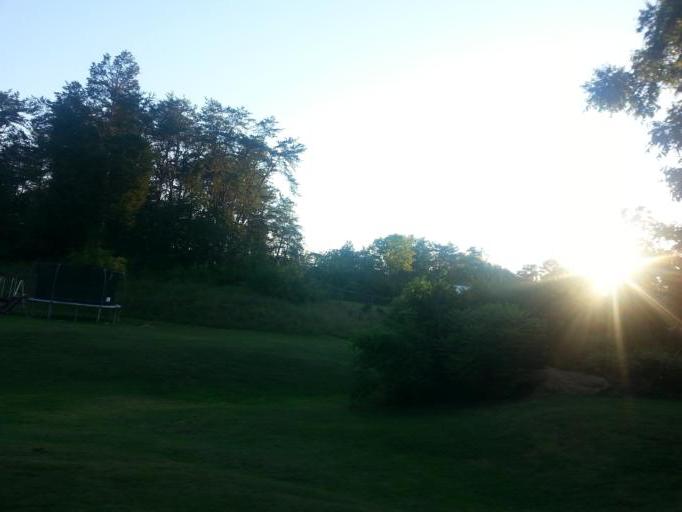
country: US
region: Tennessee
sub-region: Sevier County
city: Seymour
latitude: 35.9019
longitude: -83.8169
